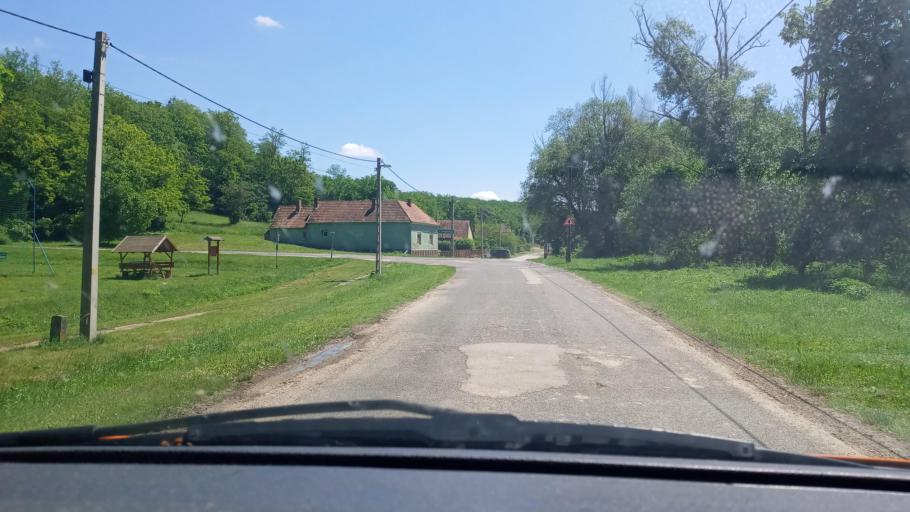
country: HU
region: Somogy
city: Kadarkut
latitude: 46.1801
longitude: 17.7260
